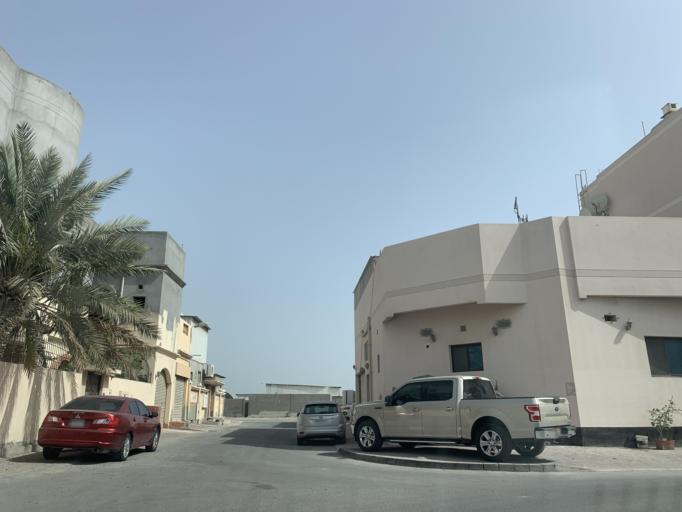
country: BH
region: Northern
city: Sitrah
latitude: 26.1356
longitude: 50.5964
